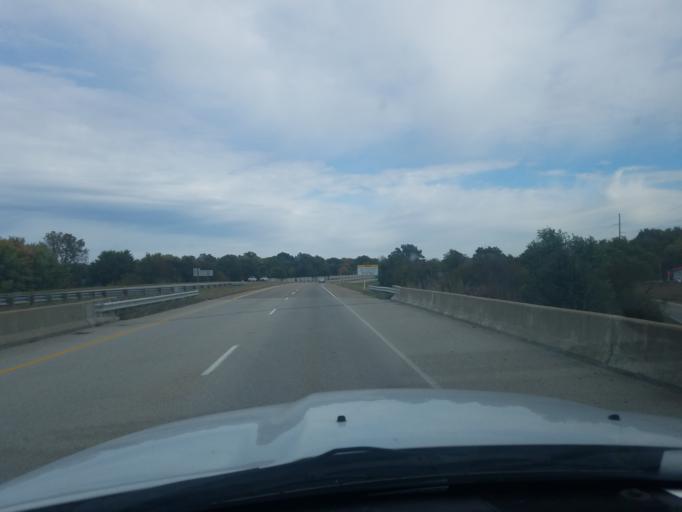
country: US
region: Indiana
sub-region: Warrick County
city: Newburgh
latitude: 37.9475
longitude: -87.4709
